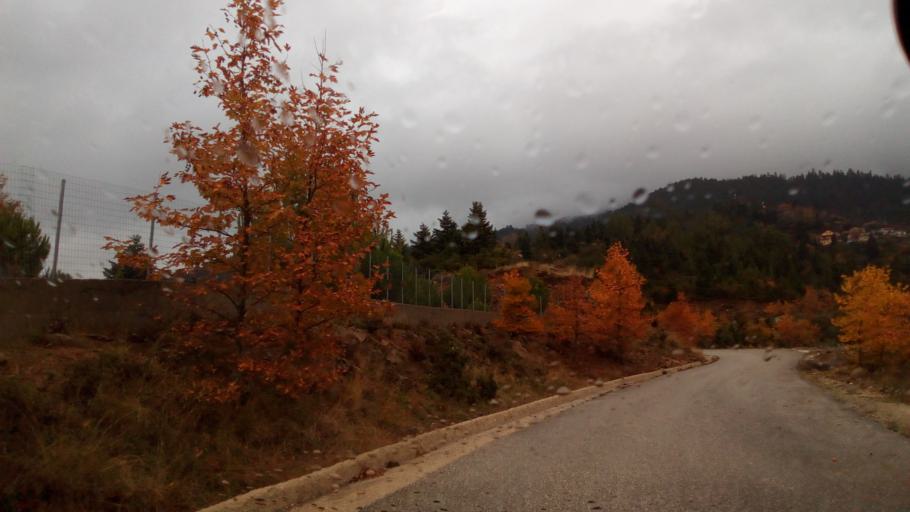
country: GR
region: West Greece
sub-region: Nomos Aitolias kai Akarnanias
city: Thermo
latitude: 38.6845
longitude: 21.8573
